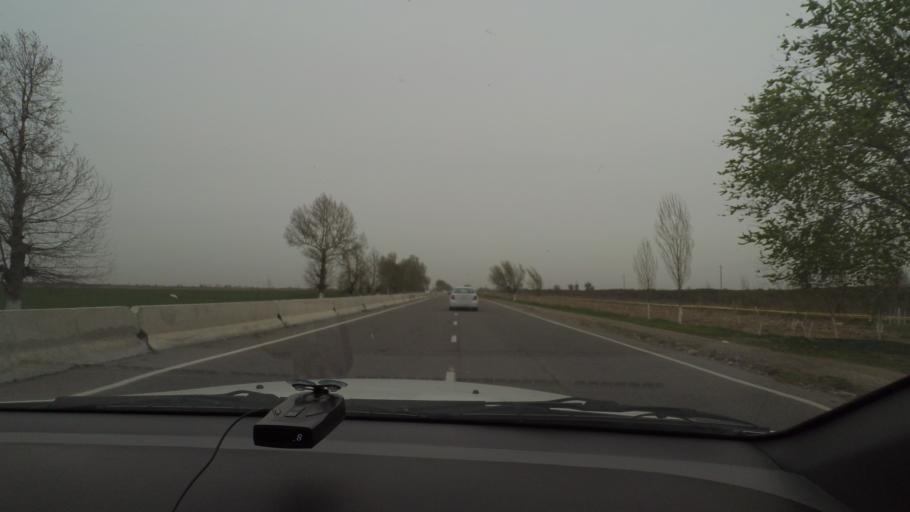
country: UZ
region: Jizzax
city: Gagarin
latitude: 40.5339
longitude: 68.3448
